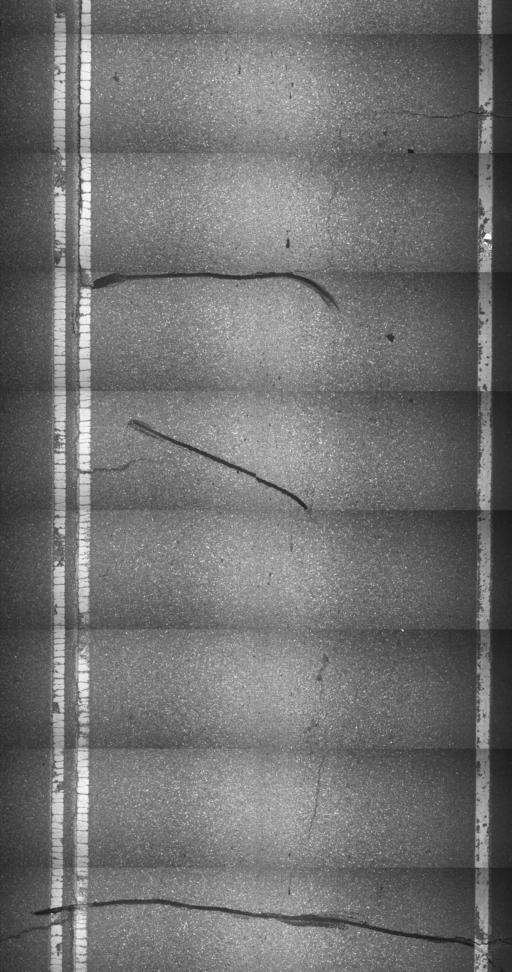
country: US
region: Vermont
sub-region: Orleans County
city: Newport
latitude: 44.7183
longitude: -72.1848
